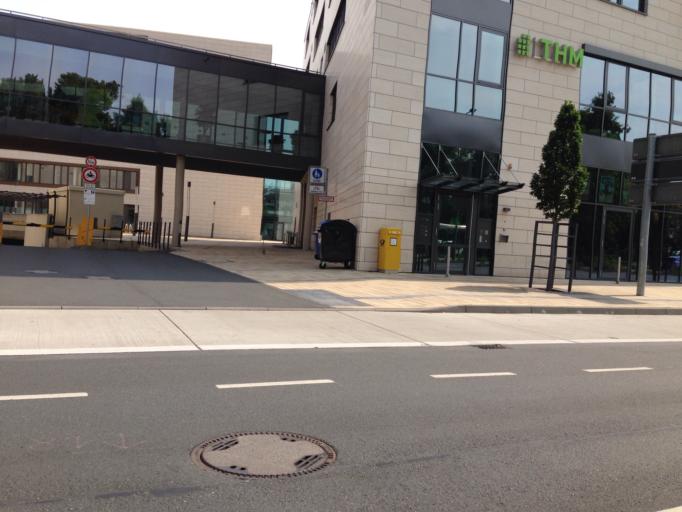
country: DE
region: Hesse
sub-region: Regierungsbezirk Giessen
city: Giessen
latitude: 50.5847
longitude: 8.6792
